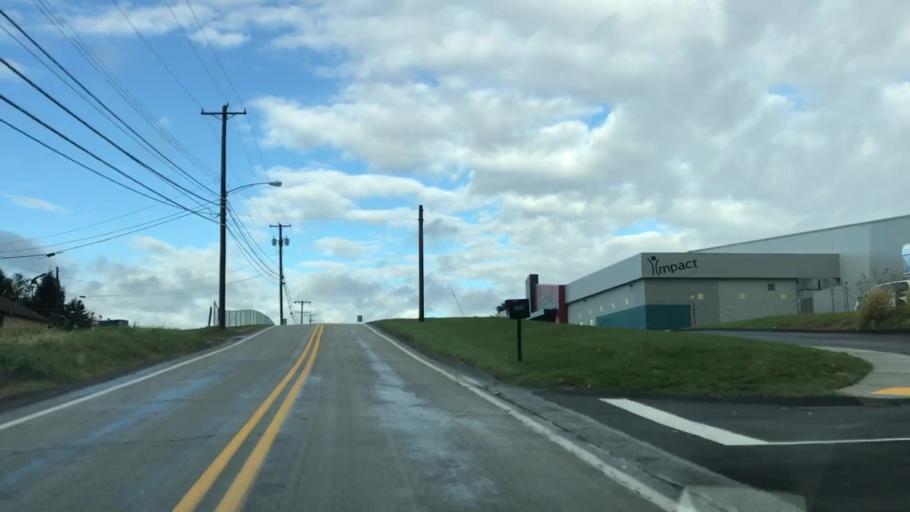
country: US
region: Pennsylvania
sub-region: Allegheny County
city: Enlow
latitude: 40.4774
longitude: -80.1930
